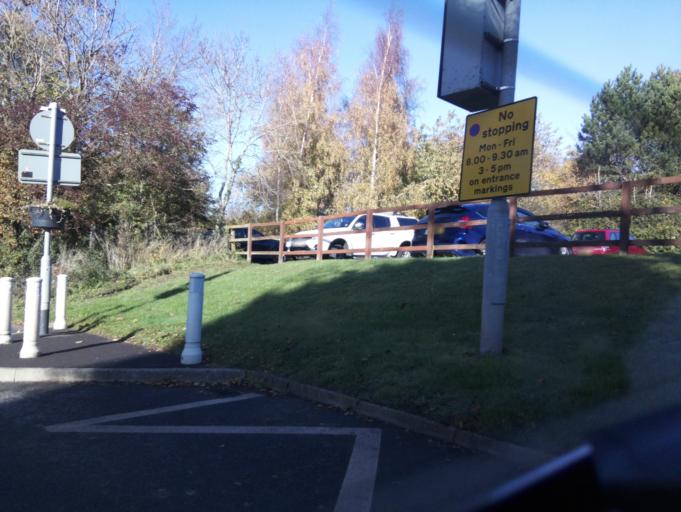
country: GB
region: England
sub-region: Somerset
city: Martock
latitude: 50.9838
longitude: -2.7531
